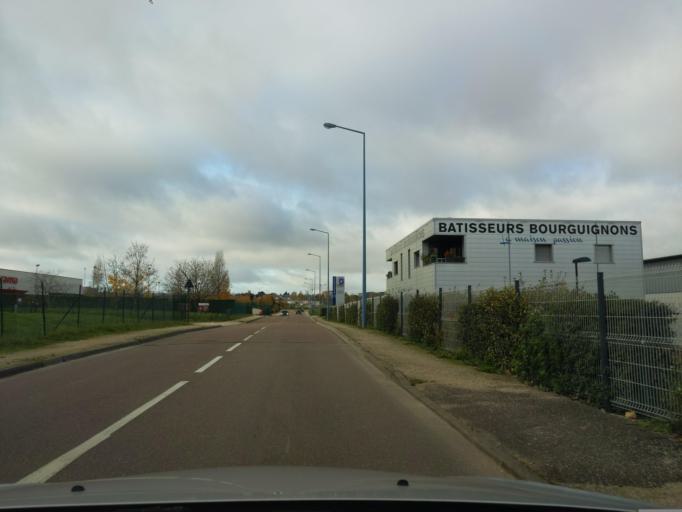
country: FR
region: Bourgogne
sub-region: Departement de la Cote-d'Or
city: Saint-Apollinaire
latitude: 47.3167
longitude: 5.0913
